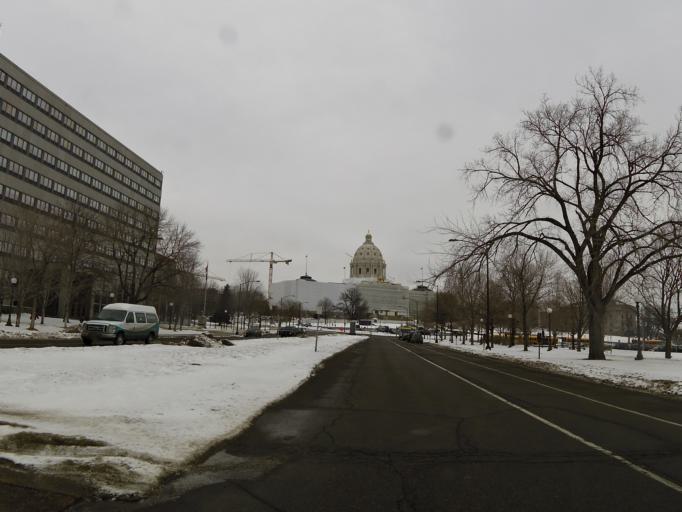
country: US
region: Minnesota
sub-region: Ramsey County
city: Saint Paul
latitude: 44.9524
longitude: -93.1044
